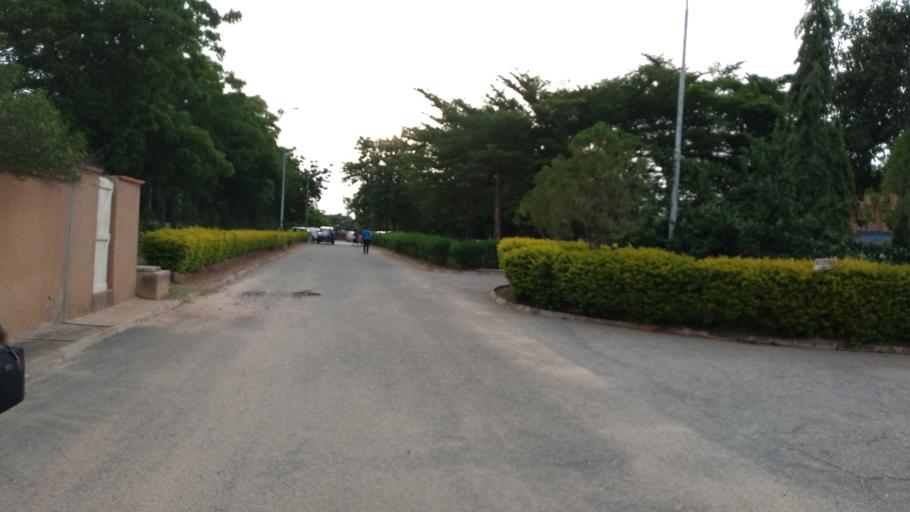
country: NG
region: Katsina
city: Katsina
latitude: 12.9624
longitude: 7.6381
